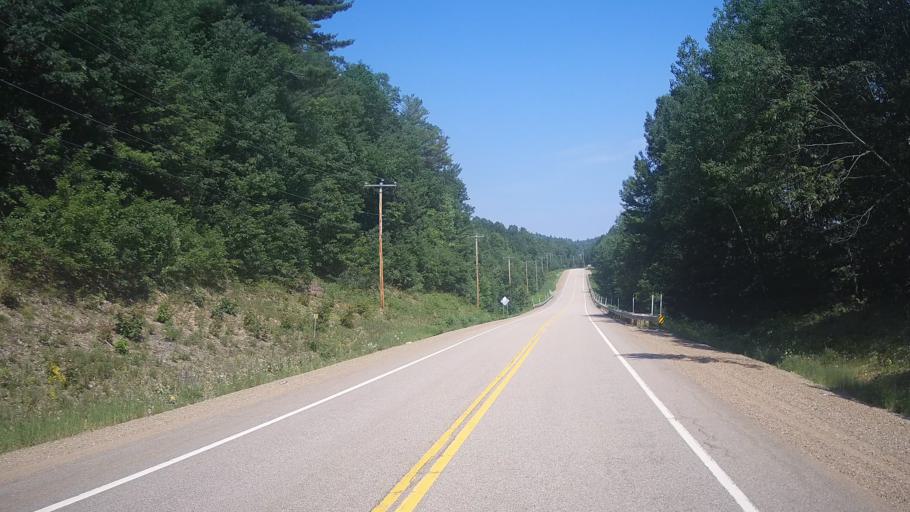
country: CA
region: Ontario
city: Pembroke
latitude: 45.9175
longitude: -76.9369
